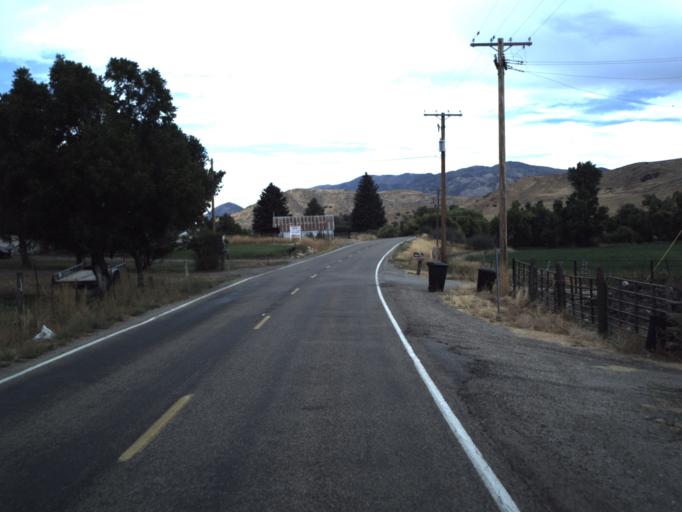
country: US
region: Utah
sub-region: Morgan County
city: Morgan
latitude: 40.9715
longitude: -111.6729
